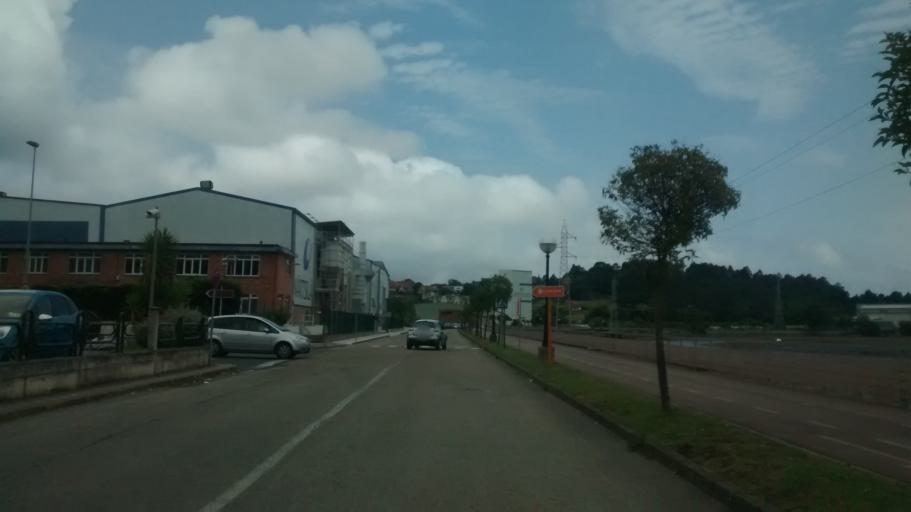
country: ES
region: Cantabria
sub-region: Provincia de Cantabria
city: El Astillero
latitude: 43.4089
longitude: -3.8290
